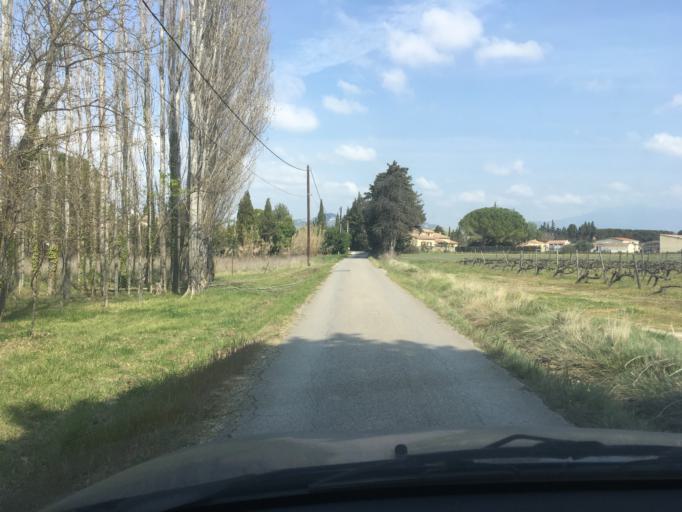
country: FR
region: Provence-Alpes-Cote d'Azur
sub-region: Departement du Vaucluse
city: Aubignan
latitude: 44.0890
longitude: 5.0141
